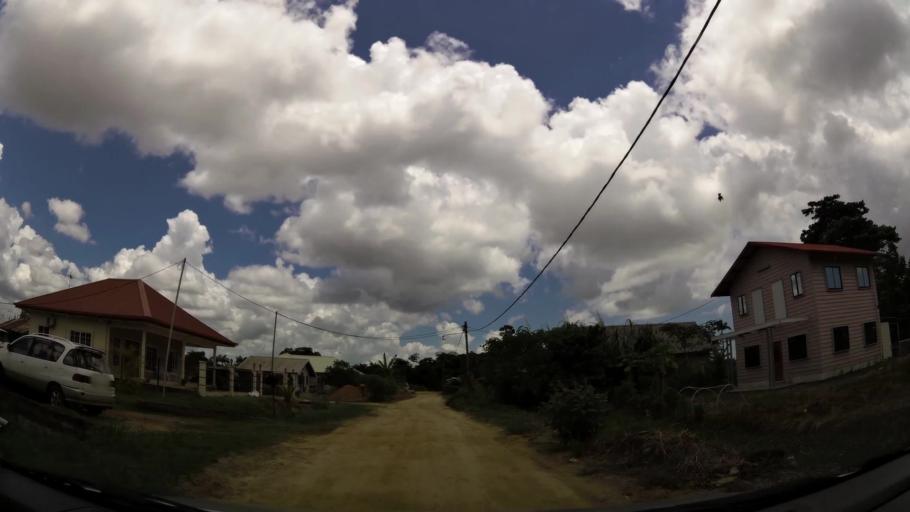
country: SR
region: Paramaribo
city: Paramaribo
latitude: 5.8606
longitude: -55.1556
